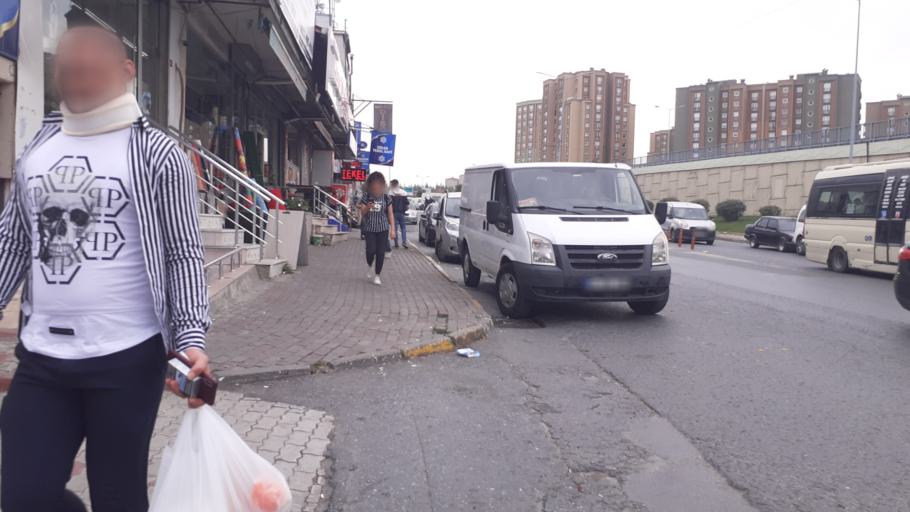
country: TR
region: Istanbul
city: Mahmutbey
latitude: 41.0536
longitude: 28.7929
